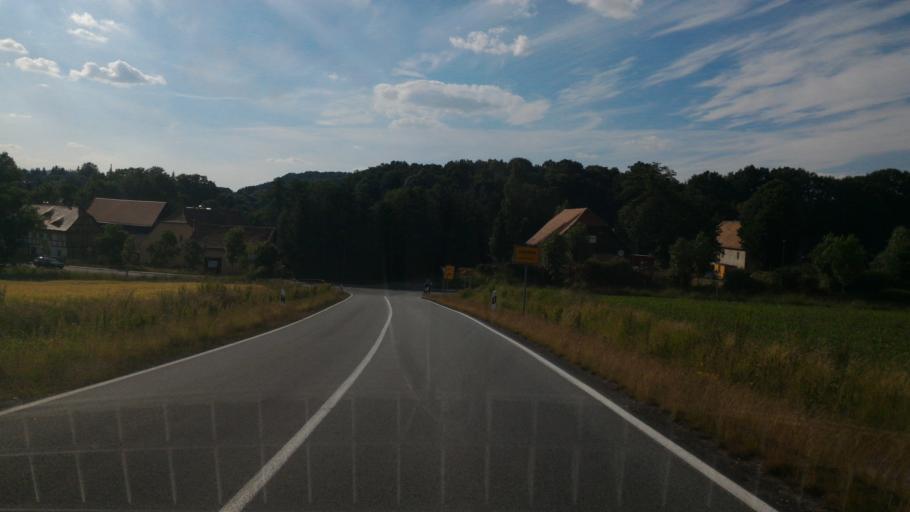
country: DE
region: Saxony
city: Grossschonau
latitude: 50.8922
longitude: 14.6866
